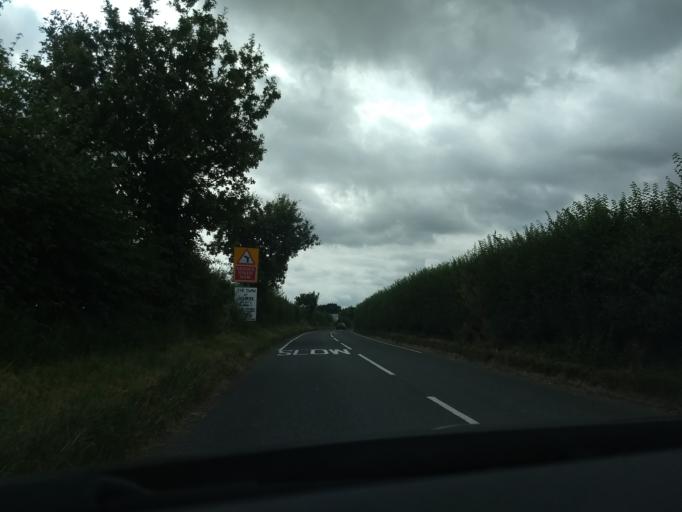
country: GB
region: England
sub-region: Suffolk
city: Ipswich
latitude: 52.0081
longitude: 1.1659
